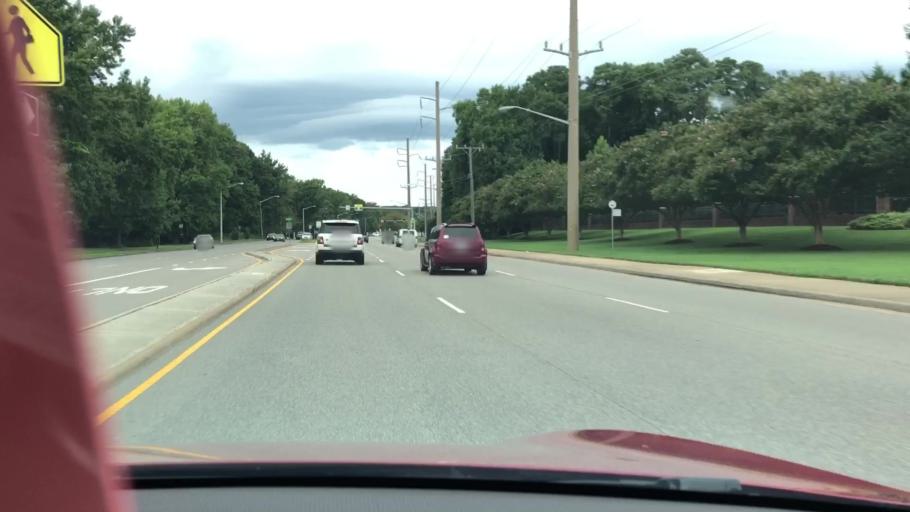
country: US
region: Virginia
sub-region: City of Virginia Beach
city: Virginia Beach
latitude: 36.8840
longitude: -76.0470
